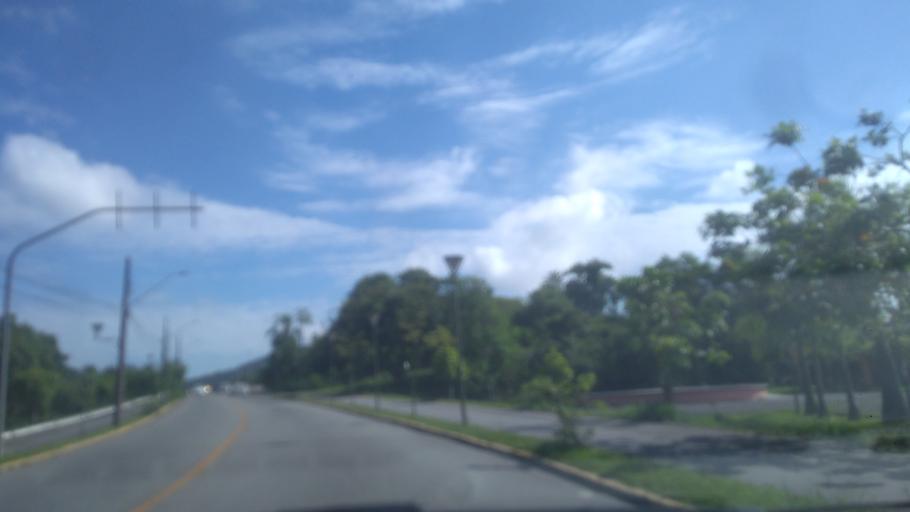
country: BR
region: Santa Catarina
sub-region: Joinville
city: Joinville
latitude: -26.3157
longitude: -48.8281
